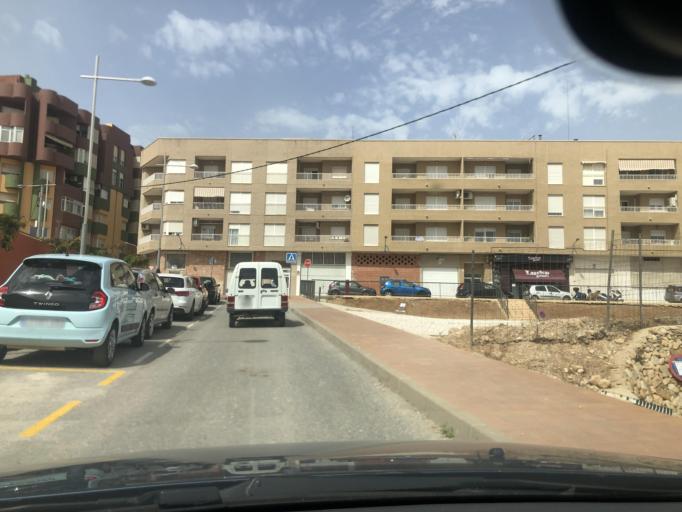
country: ES
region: Valencia
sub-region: Provincia de Alicante
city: Callosa d'En Sarria
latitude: 38.6492
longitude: -0.1191
